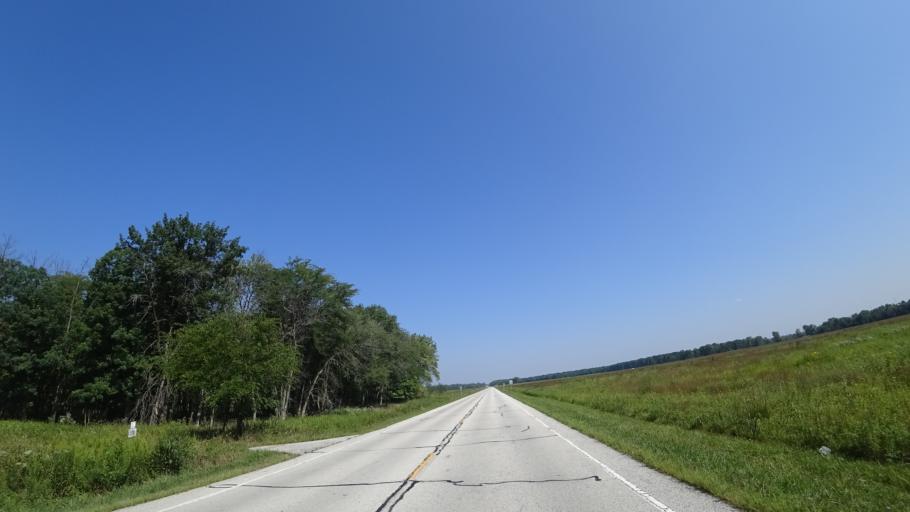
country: US
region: Illinois
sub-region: Cook County
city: Country Club Hills
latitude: 41.5373
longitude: -87.7518
